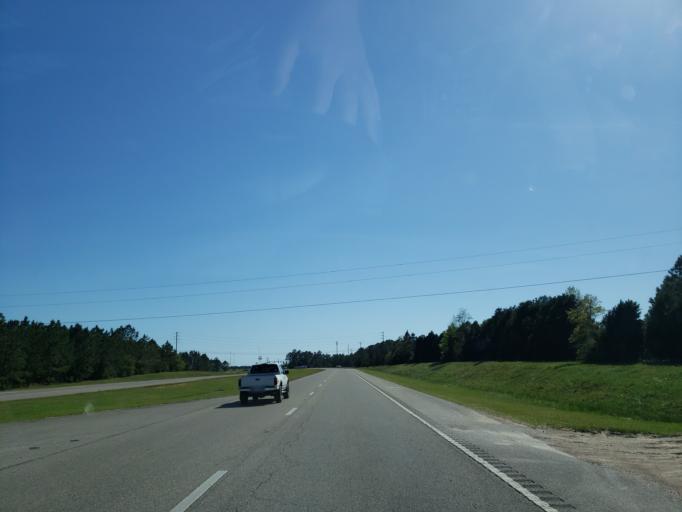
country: US
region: Mississippi
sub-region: Harrison County
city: West Gulfport
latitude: 30.4539
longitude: -89.0293
